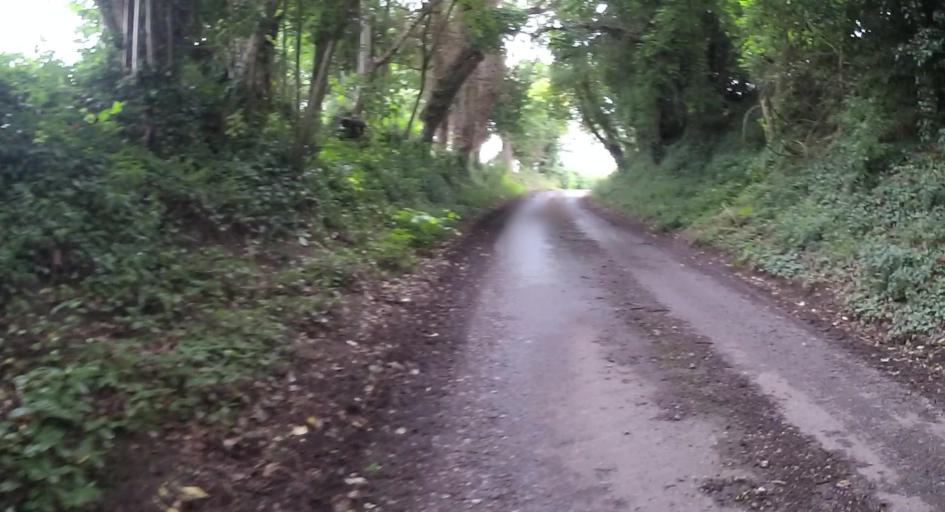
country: GB
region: England
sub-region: Hampshire
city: Highclere
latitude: 51.2557
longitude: -1.4123
